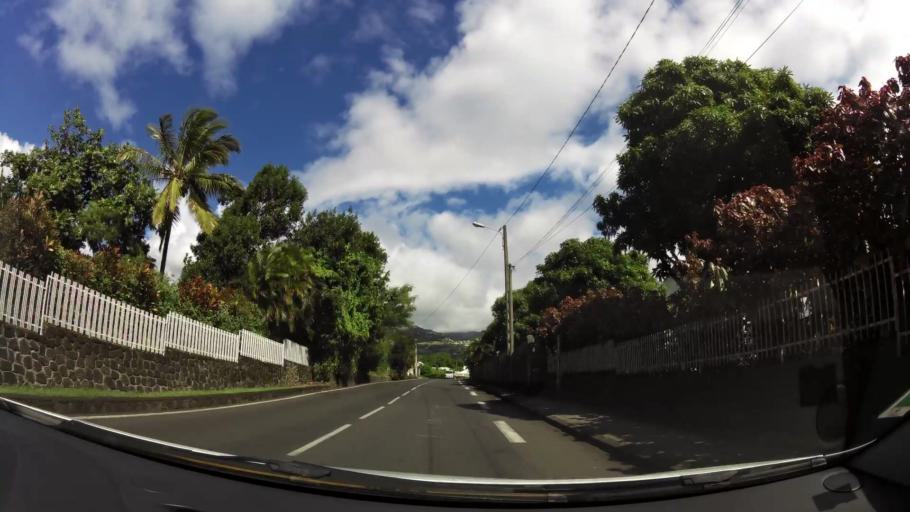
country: RE
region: Reunion
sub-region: Reunion
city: Sainte-Marie
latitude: -20.9138
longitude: 55.4965
